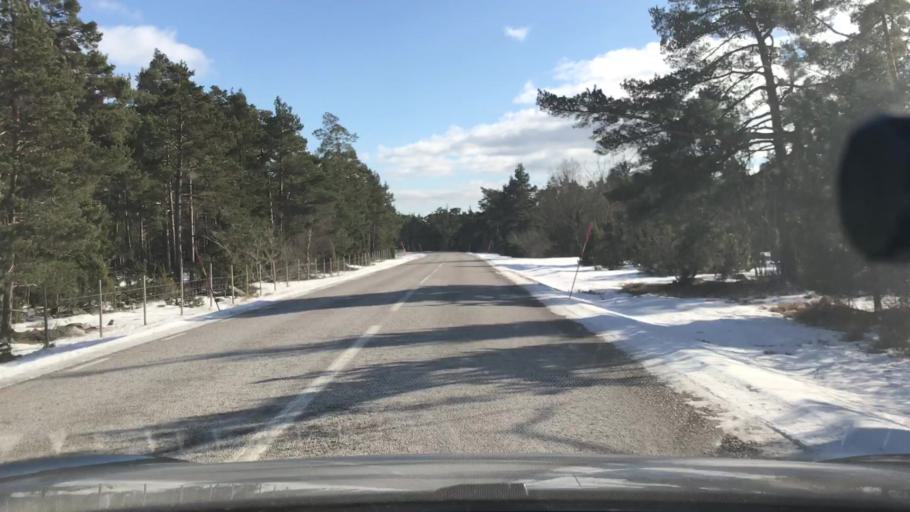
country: SE
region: Gotland
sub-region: Gotland
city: Hemse
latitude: 57.3517
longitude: 18.6876
